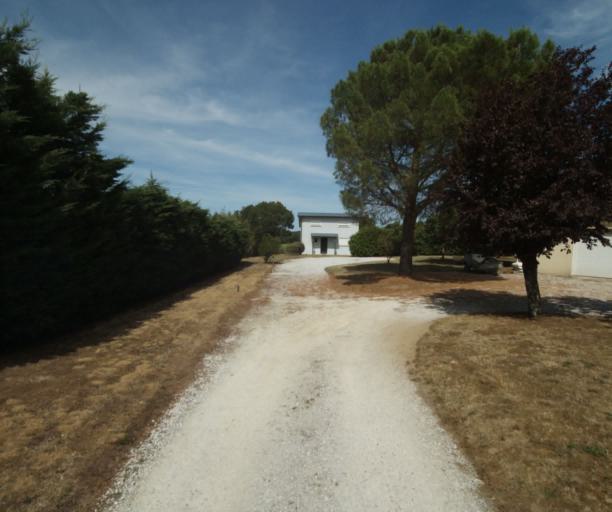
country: FR
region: Midi-Pyrenees
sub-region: Departement de la Haute-Garonne
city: Revel
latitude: 43.5121
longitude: 2.0333
